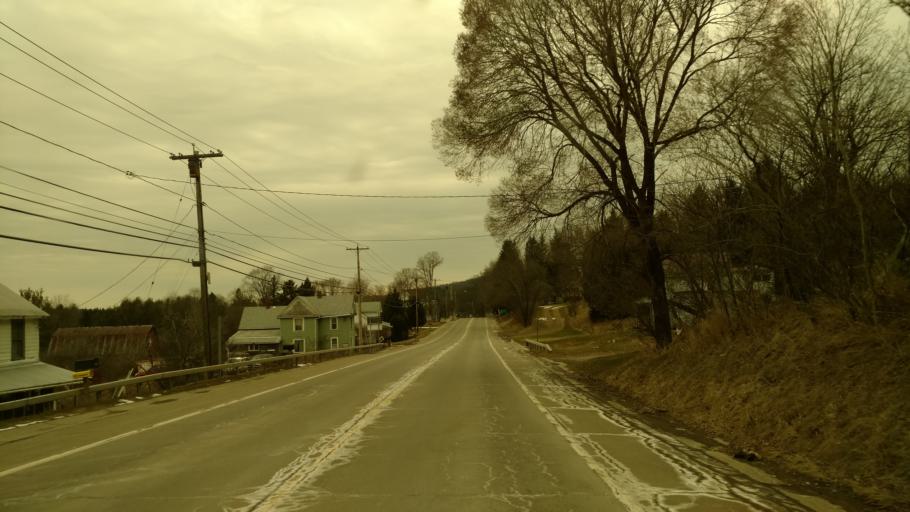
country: US
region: New York
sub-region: Allegany County
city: Wellsville
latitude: 42.1089
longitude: -77.9310
